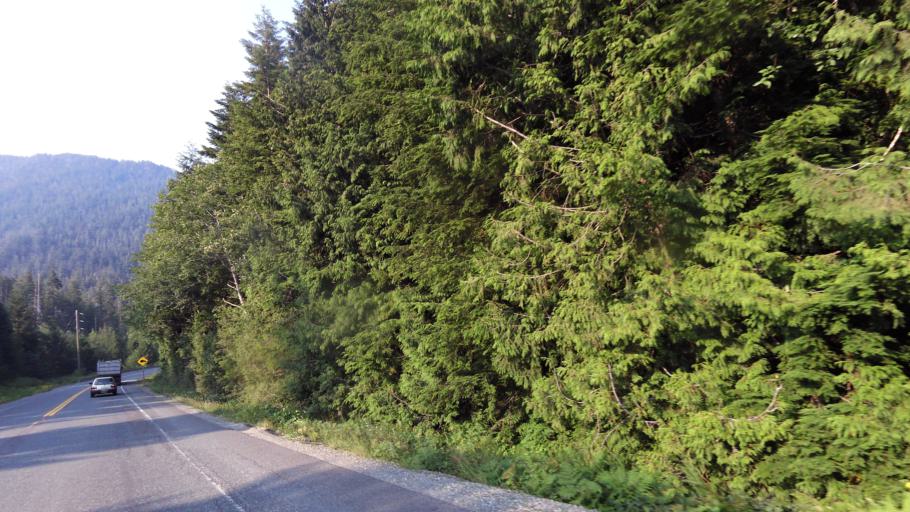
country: CA
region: British Columbia
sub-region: Regional District of Alberni-Clayoquot
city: Ucluelet
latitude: 49.2729
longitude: -125.3646
